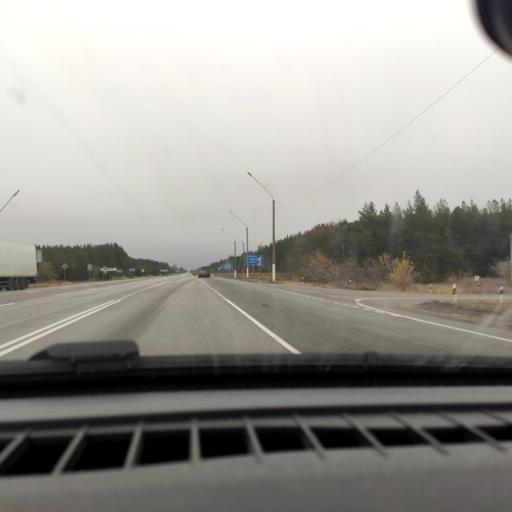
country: RU
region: Voronezj
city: Uryv-Pokrovka
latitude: 51.0469
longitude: 38.9824
